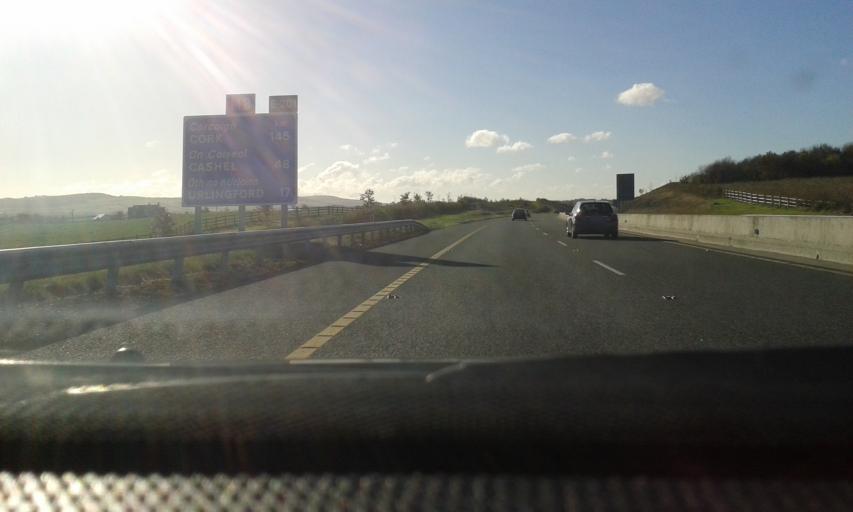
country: IE
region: Leinster
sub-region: Laois
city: Rathdowney
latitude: 52.8574
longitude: -7.4862
